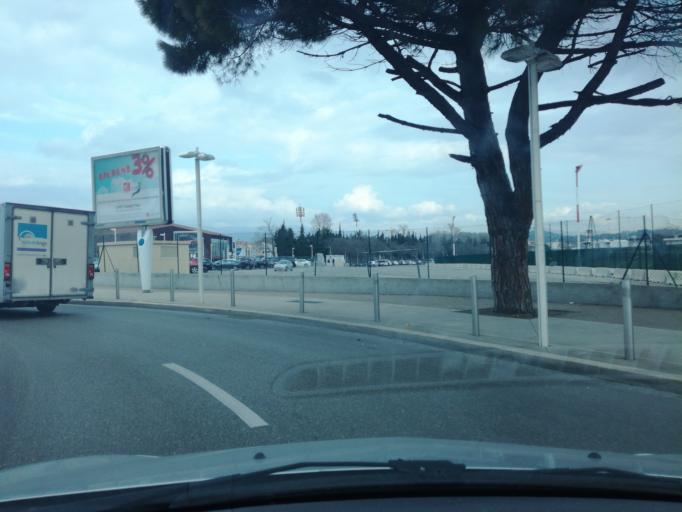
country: FR
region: Provence-Alpes-Cote d'Azur
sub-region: Departement des Alpes-Maritimes
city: Mandelieu-la-Napoule
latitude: 43.5501
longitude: 6.9626
